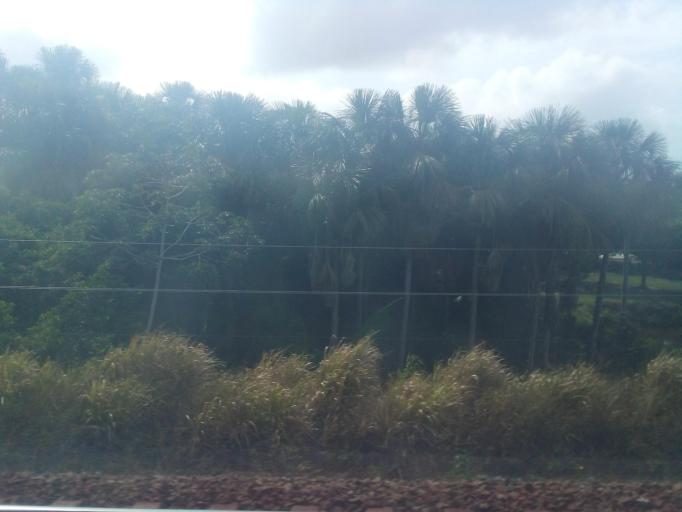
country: BR
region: Maranhao
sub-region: Sao Luis
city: Sao Luis
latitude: -2.7288
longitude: -44.3348
